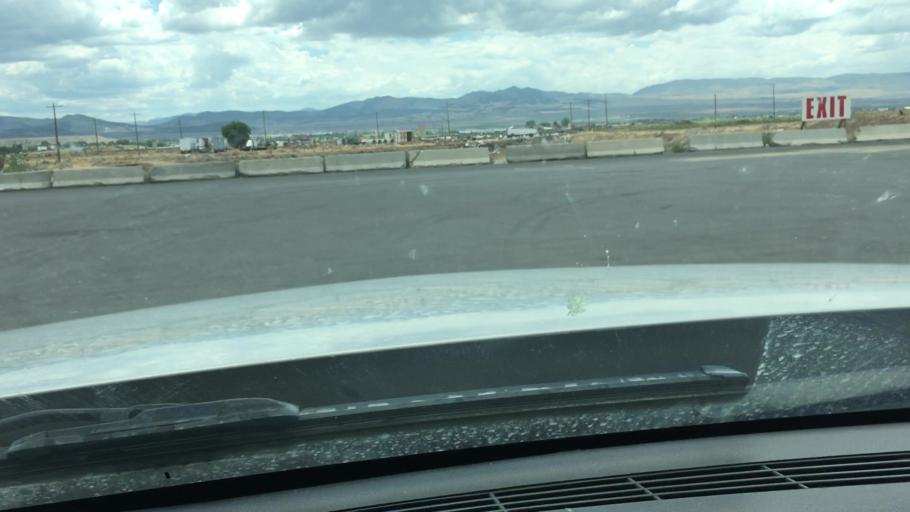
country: US
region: Utah
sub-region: Beaver County
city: Beaver
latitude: 38.2920
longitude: -112.6536
